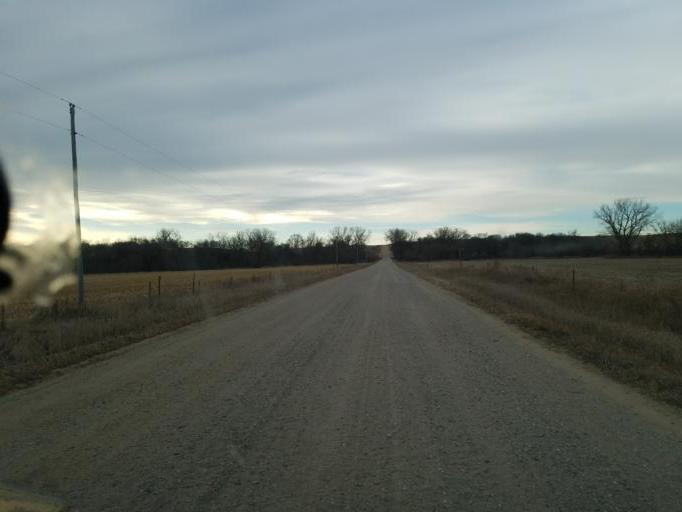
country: US
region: Nebraska
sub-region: Knox County
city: Bloomfield
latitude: 42.5533
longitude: -97.7597
